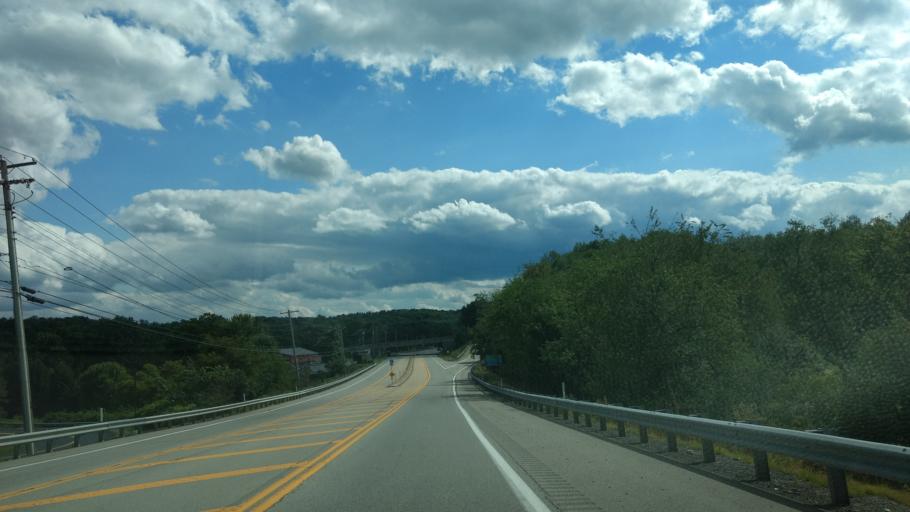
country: US
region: Pennsylvania
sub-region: Armstrong County
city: Apollo
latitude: 40.5311
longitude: -79.5967
